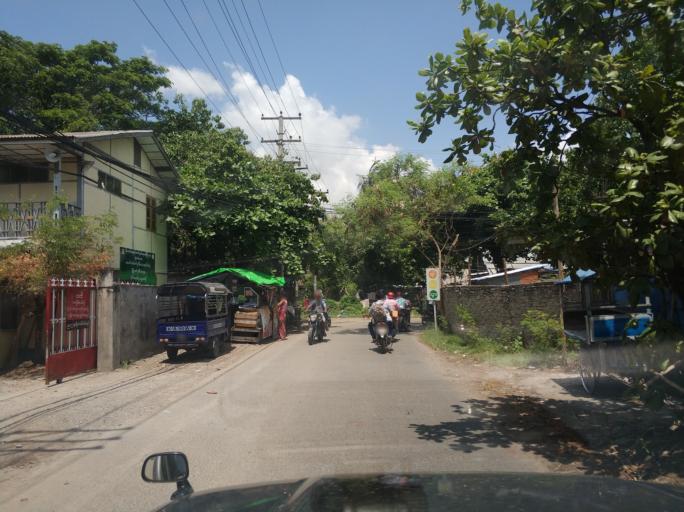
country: MM
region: Mandalay
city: Mandalay
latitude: 21.9815
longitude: 96.0868
